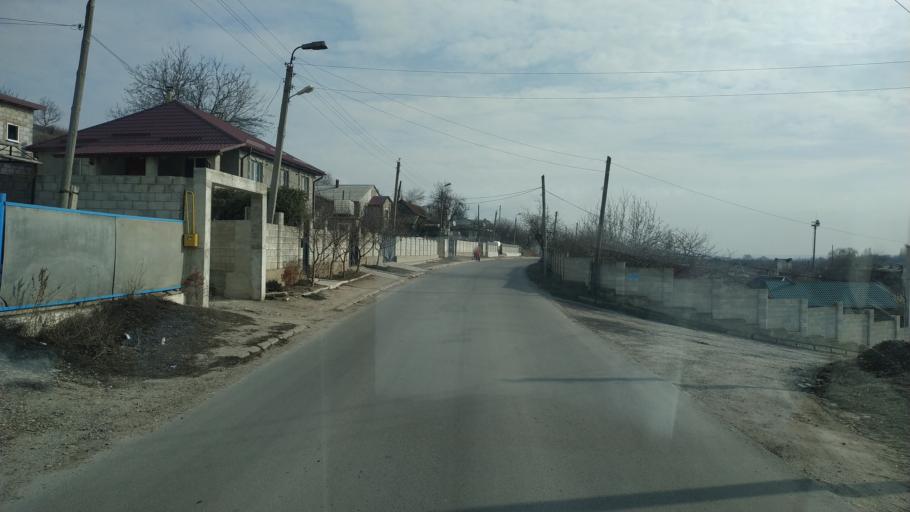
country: MD
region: Chisinau
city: Singera
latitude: 46.9245
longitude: 29.0624
